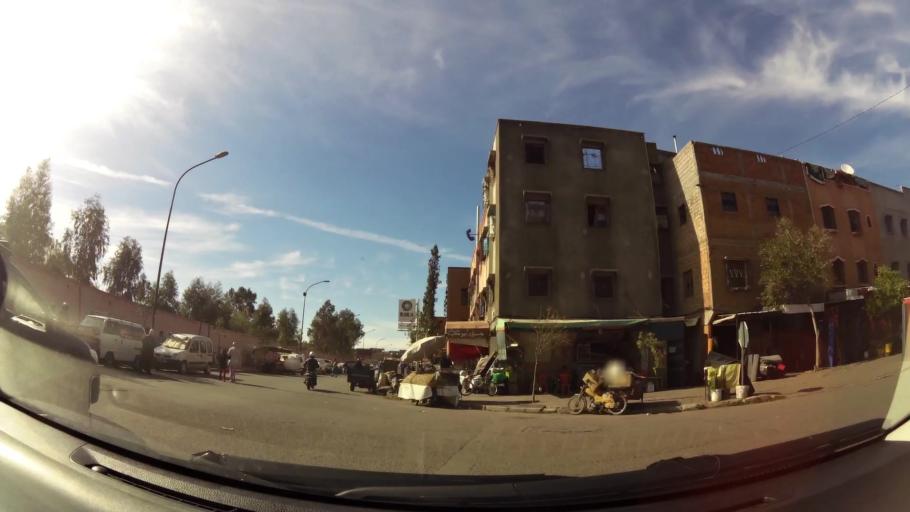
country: MA
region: Marrakech-Tensift-Al Haouz
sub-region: Marrakech
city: Marrakesh
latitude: 31.6061
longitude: -7.9633
